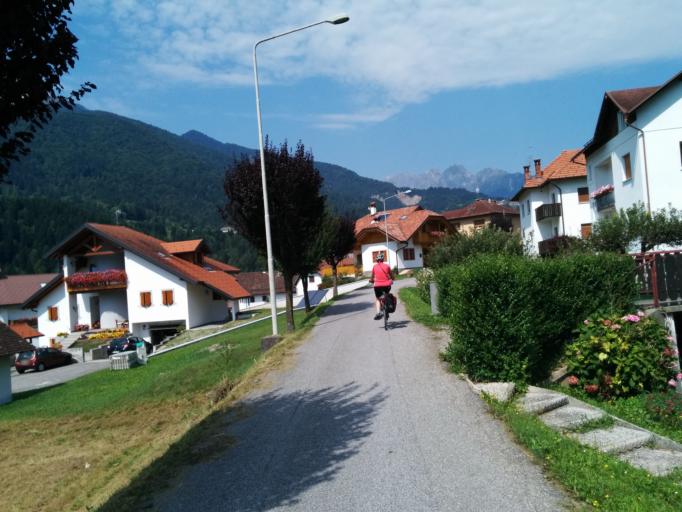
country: IT
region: Friuli Venezia Giulia
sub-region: Provincia di Udine
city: Ovaro
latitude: 46.4801
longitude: 12.8684
